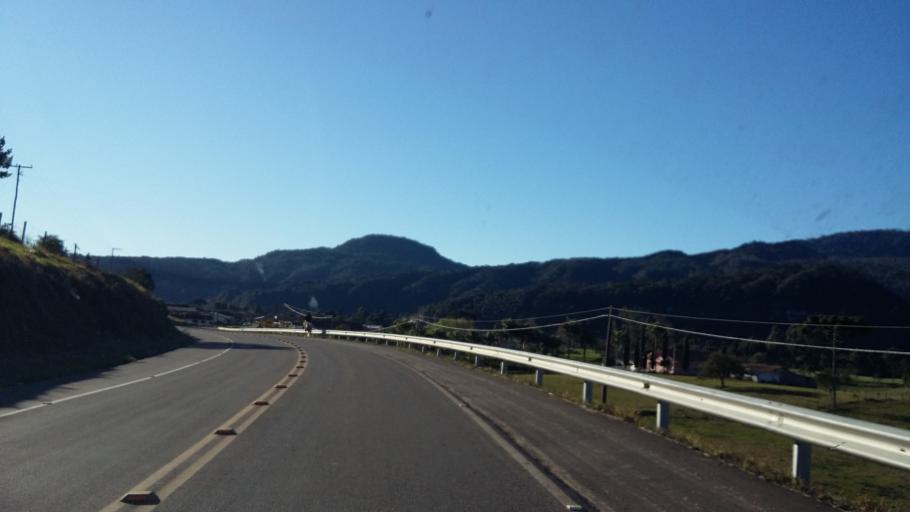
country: BR
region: Santa Catarina
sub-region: Lauro Muller
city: Lauro Muller
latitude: -28.0261
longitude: -49.4972
